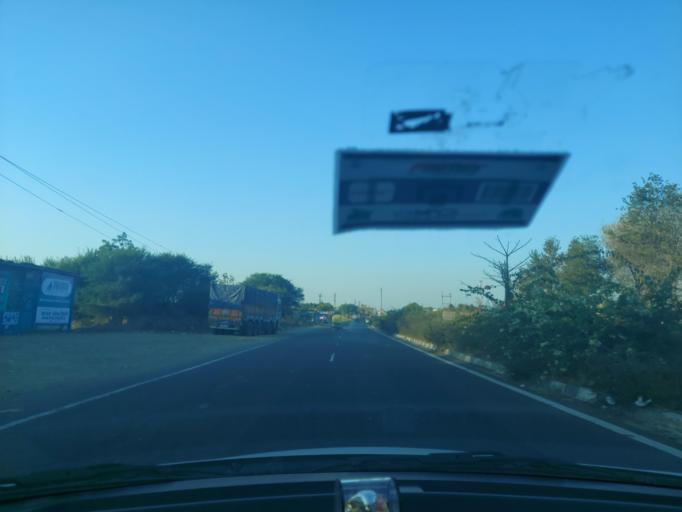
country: IN
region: Madhya Pradesh
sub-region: Ujjain
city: Ujjain
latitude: 23.0857
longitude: 75.8170
